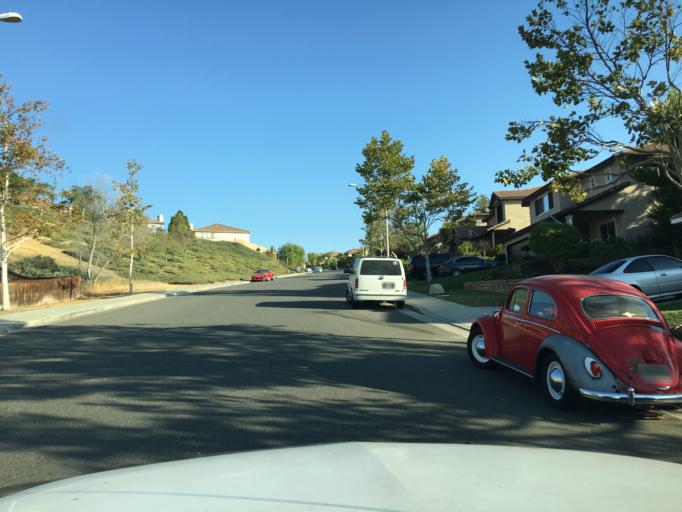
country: US
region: California
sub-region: Los Angeles County
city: Castaic
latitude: 34.5133
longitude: -118.6390
